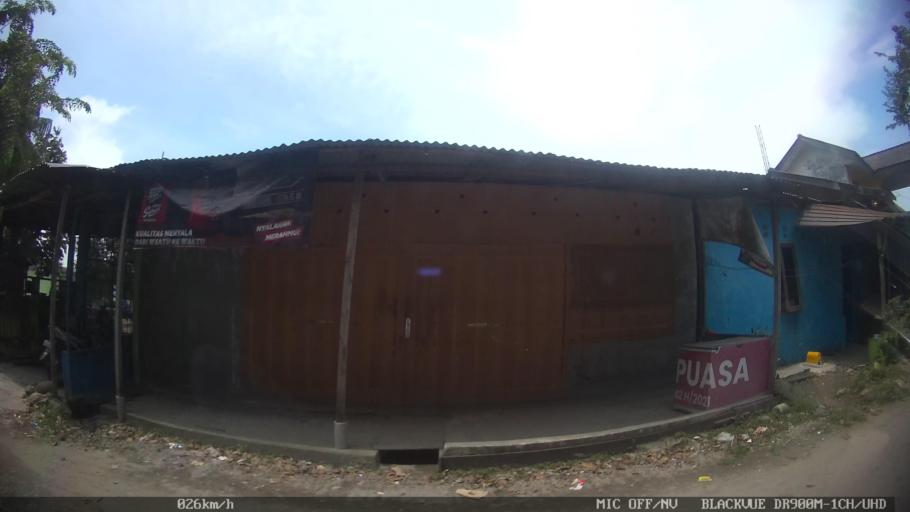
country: ID
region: North Sumatra
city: Labuhan Deli
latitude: 3.7080
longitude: 98.6781
